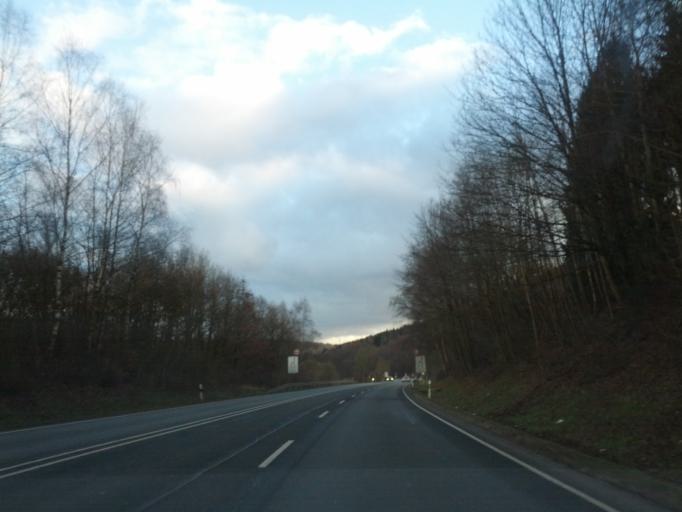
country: DE
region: Hesse
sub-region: Regierungsbezirk Kassel
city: Helsa
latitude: 51.2712
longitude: 9.6637
